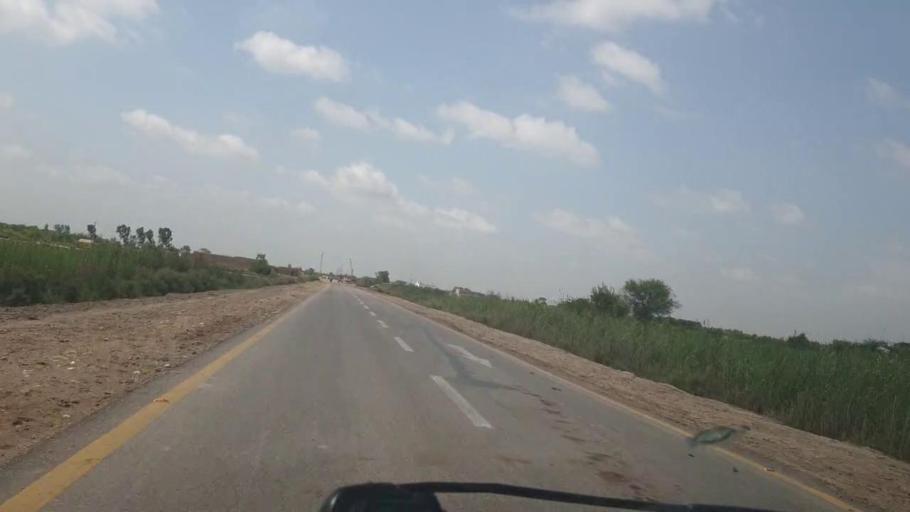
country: PK
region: Sindh
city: Berani
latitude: 25.6870
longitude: 68.9273
